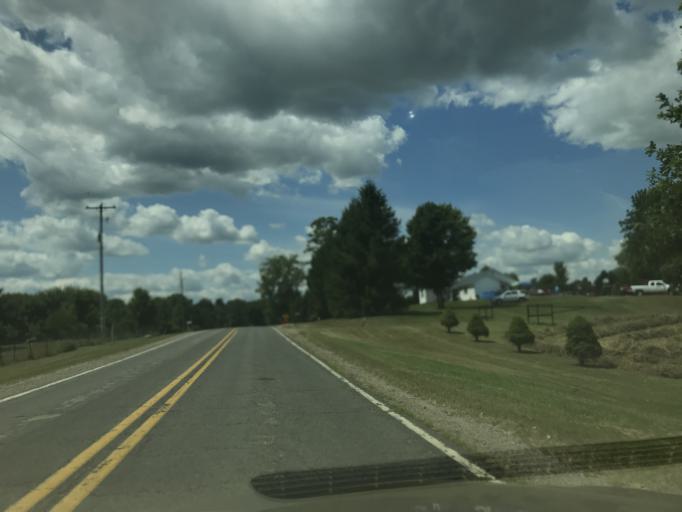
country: US
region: Michigan
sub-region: Eaton County
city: Eaton Rapids
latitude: 42.4511
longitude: -84.5573
